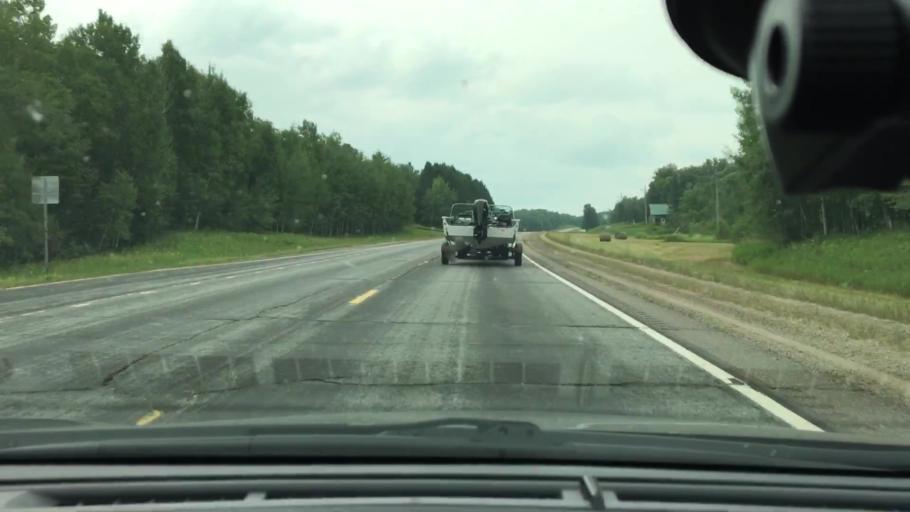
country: US
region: Minnesota
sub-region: Crow Wing County
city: Crosby
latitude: 46.6291
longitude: -93.9464
